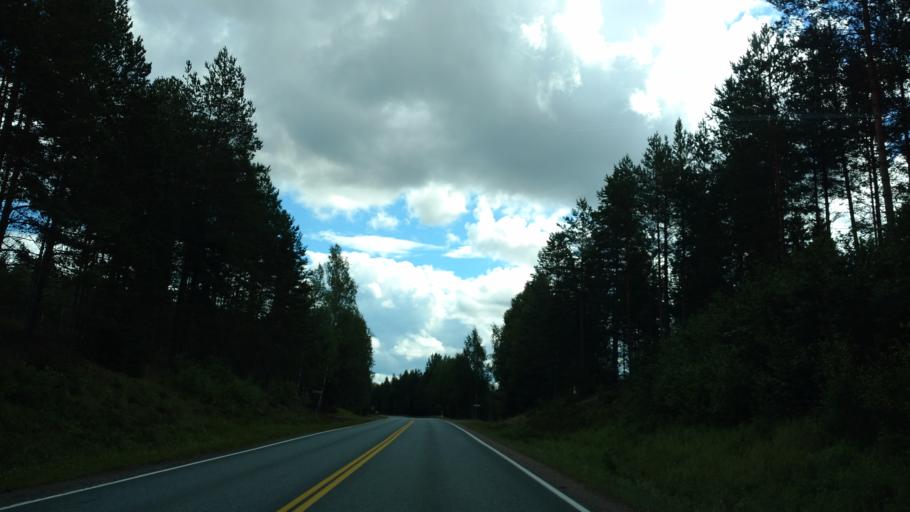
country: FI
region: Uusimaa
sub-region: Helsinki
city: Karjalohja
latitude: 60.2211
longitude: 23.6221
